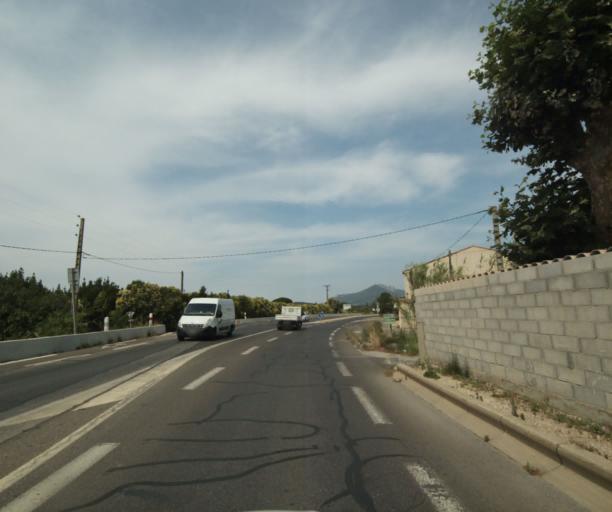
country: FR
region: Provence-Alpes-Cote d'Azur
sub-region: Departement du Var
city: La Crau
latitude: 43.1313
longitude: 6.0461
